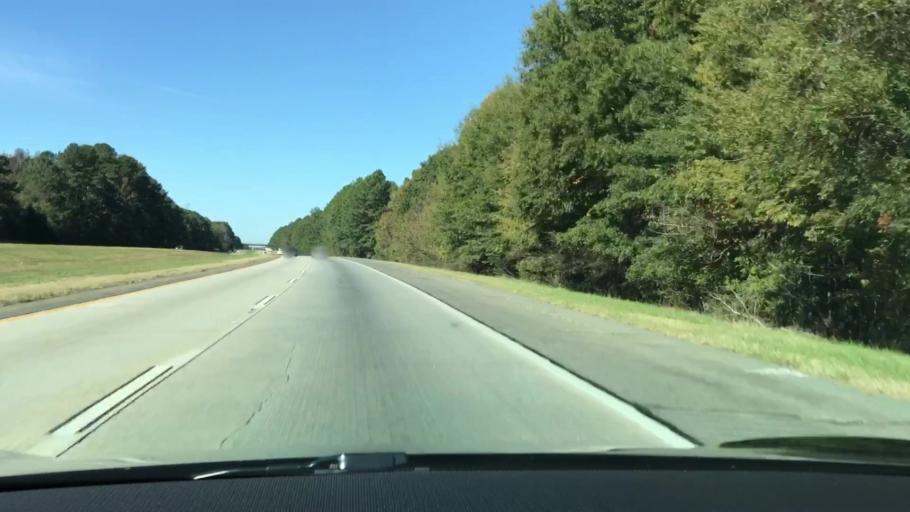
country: US
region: Georgia
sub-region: Taliaferro County
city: Crawfordville
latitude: 33.5376
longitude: -82.9980
